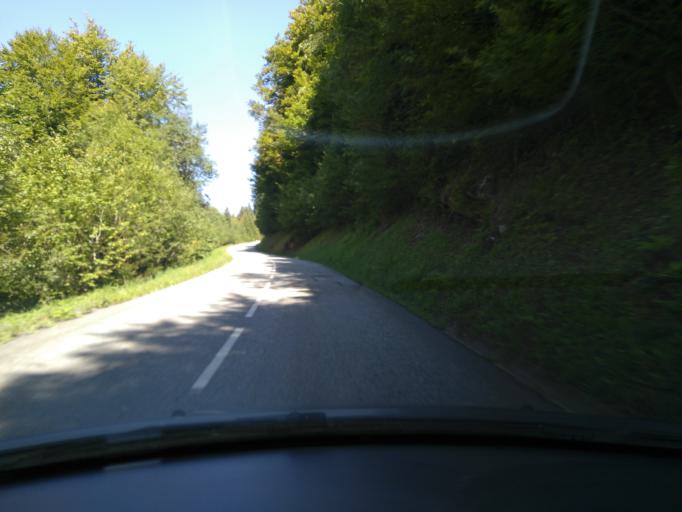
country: FR
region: Rhone-Alpes
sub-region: Departement de la Savoie
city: Ugine
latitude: 45.7929
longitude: 6.4888
